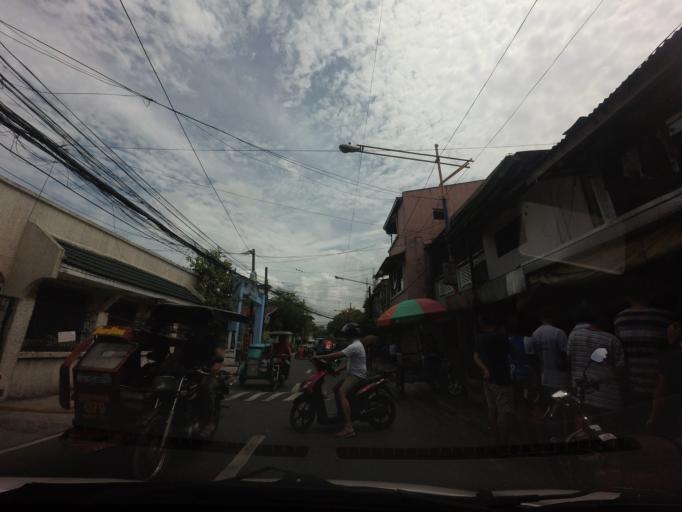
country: PH
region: Calabarzon
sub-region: Province of Rizal
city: Pateros
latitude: 14.5638
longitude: 121.0806
